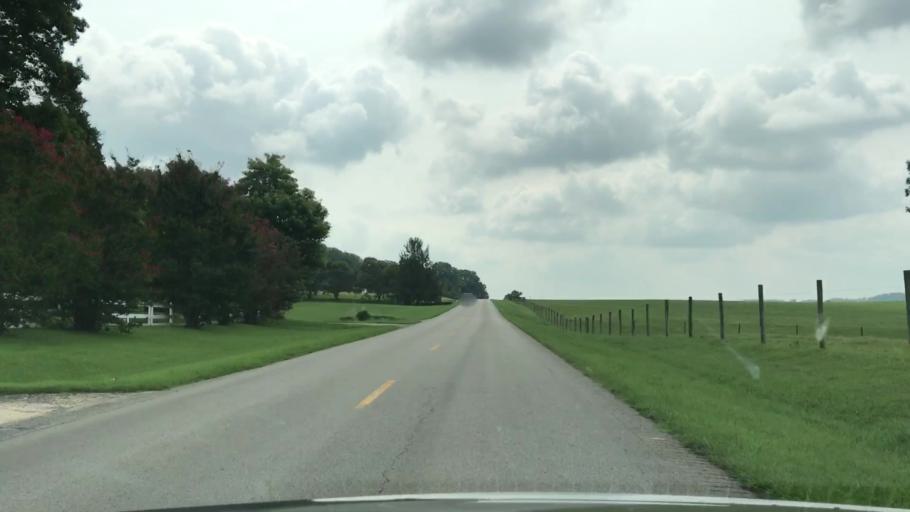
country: US
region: Kentucky
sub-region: Barren County
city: Cave City
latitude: 37.1099
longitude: -85.9851
